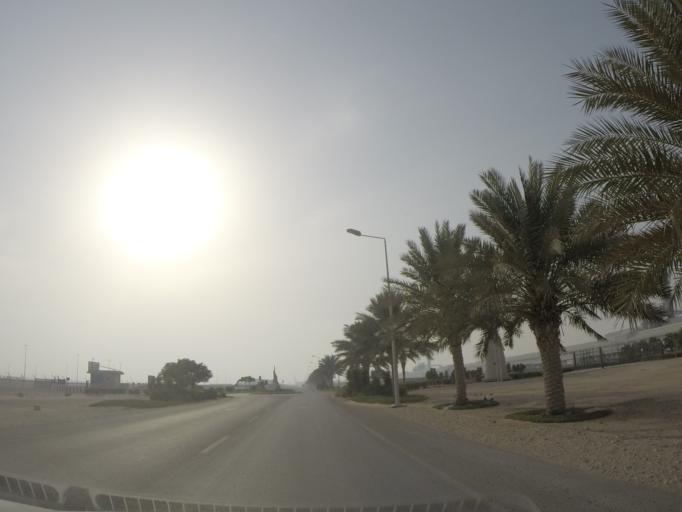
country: AE
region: Abu Dhabi
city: Abu Dhabi
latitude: 24.7815
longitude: 54.7256
